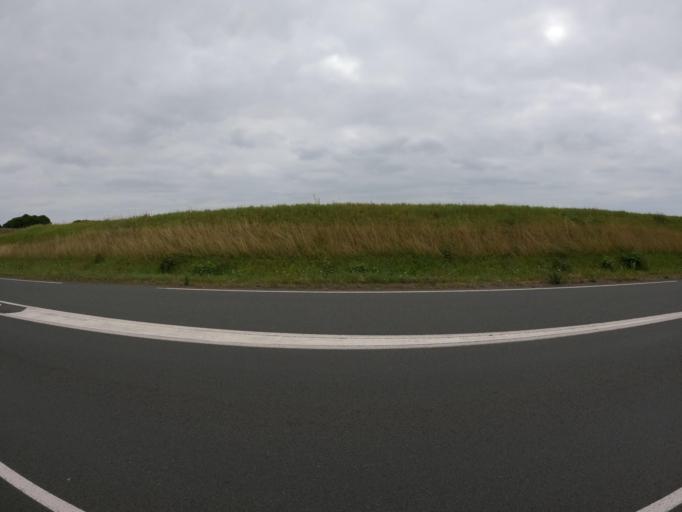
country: FR
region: Pays de la Loire
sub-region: Departement de la Vendee
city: Saint-Michel-le-Cloucq
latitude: 46.4448
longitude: -0.7606
